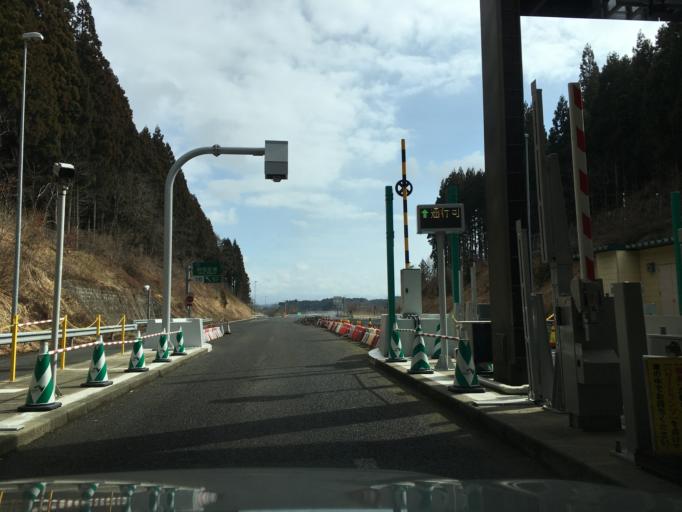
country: JP
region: Akita
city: Akita
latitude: 39.6353
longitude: 140.1788
